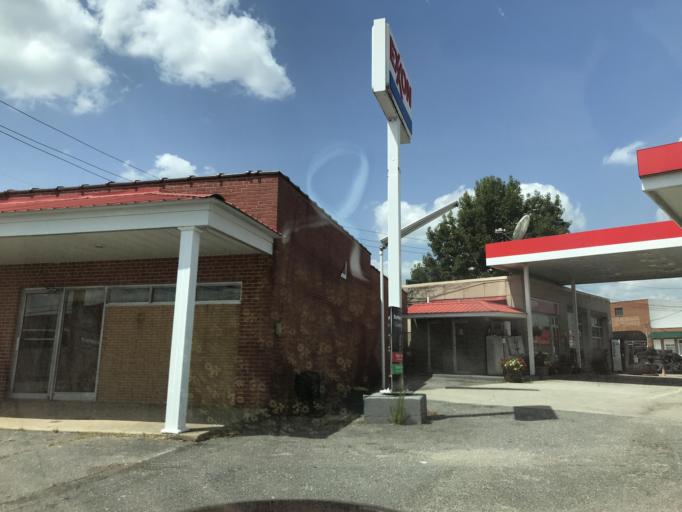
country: US
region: North Carolina
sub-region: Sampson County
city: Plain View
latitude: 35.2451
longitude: -78.3551
